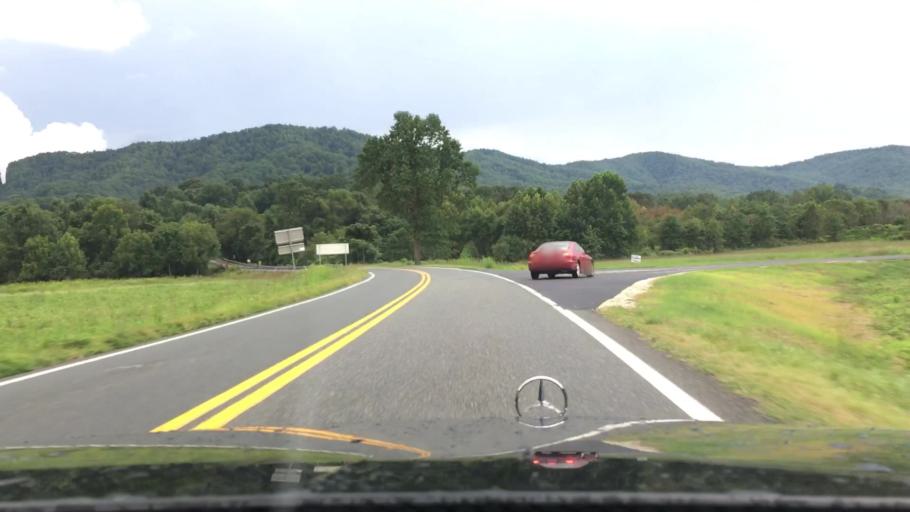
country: US
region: Virginia
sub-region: Nelson County
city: Nellysford
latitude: 37.8701
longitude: -78.9176
